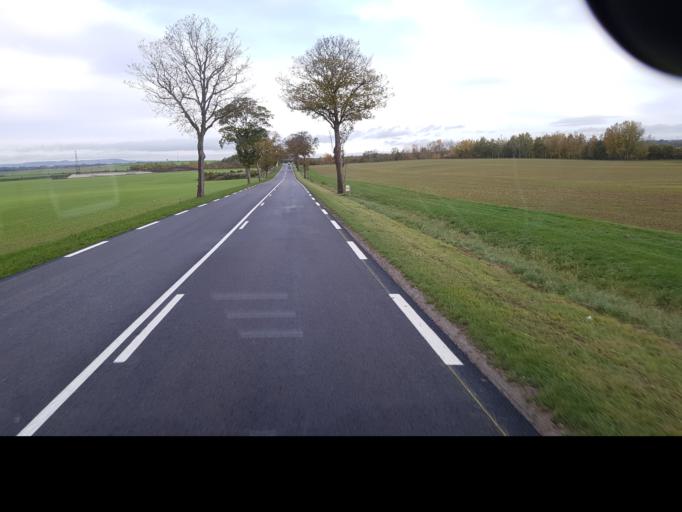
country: FR
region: Champagne-Ardenne
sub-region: Departement de l'Aube
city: Verrieres
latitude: 48.2828
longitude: 4.1745
